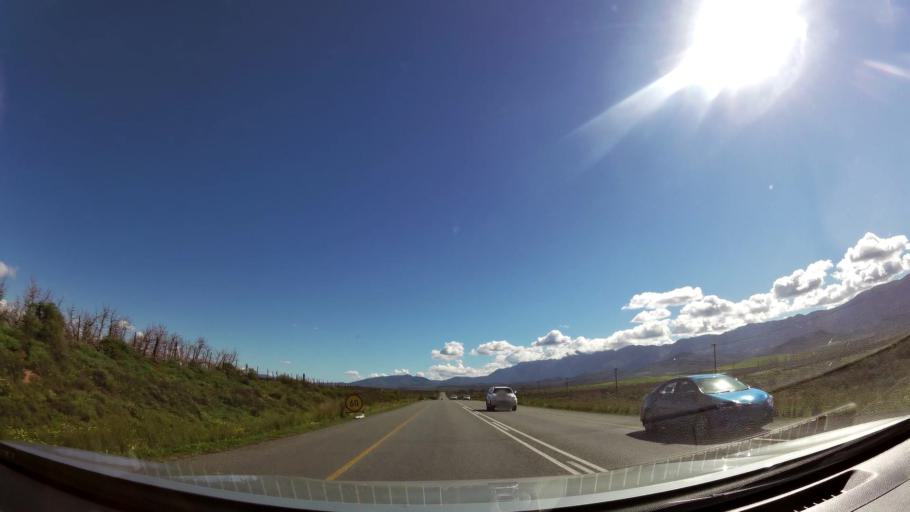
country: ZA
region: Western Cape
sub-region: Cape Winelands District Municipality
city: Ashton
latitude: -33.8357
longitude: 20.0029
